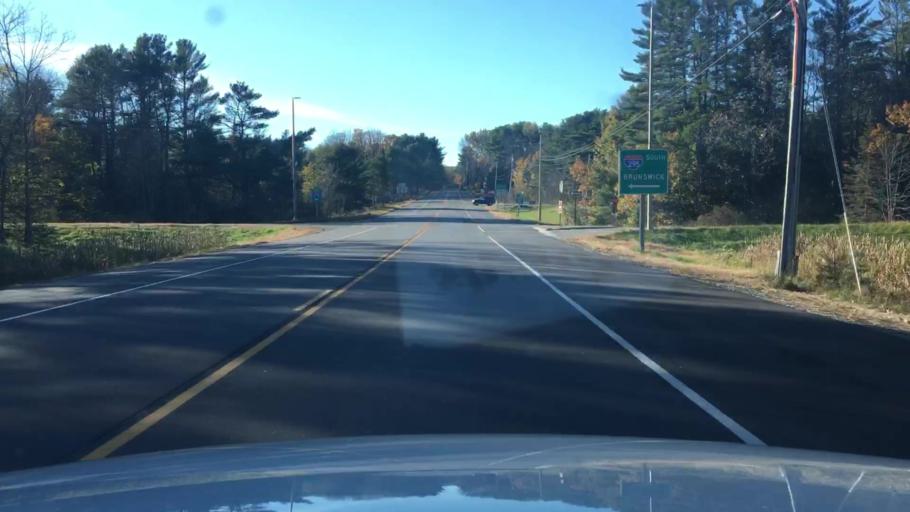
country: US
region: Maine
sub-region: Sagadahoc County
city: Topsham
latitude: 44.0173
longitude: -69.9209
